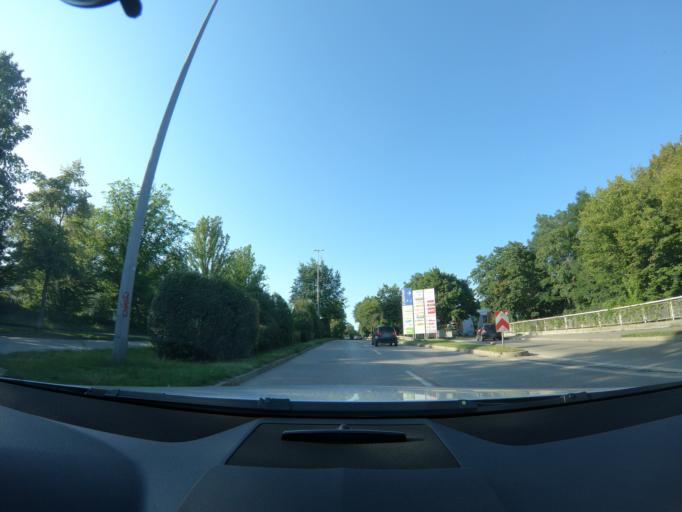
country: DE
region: Bavaria
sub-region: Upper Bavaria
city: Bogenhausen
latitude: 48.1913
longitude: 11.5842
